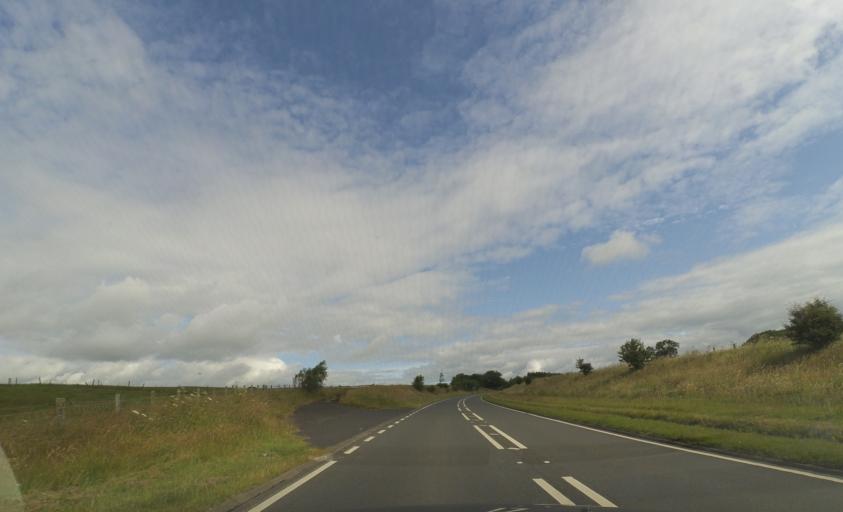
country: GB
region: Scotland
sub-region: The Scottish Borders
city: Hawick
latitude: 55.4533
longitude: -2.7795
